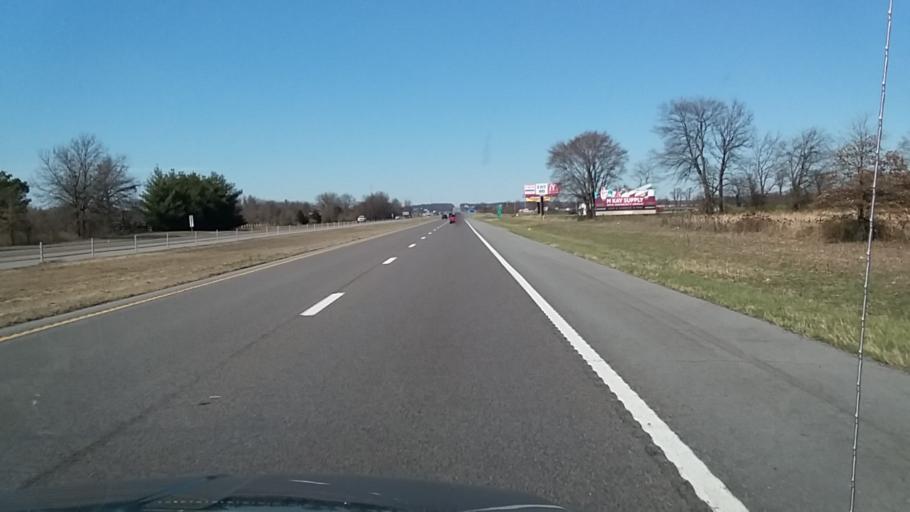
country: US
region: Missouri
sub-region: Scott County
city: Benton
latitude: 37.0709
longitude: -89.5357
